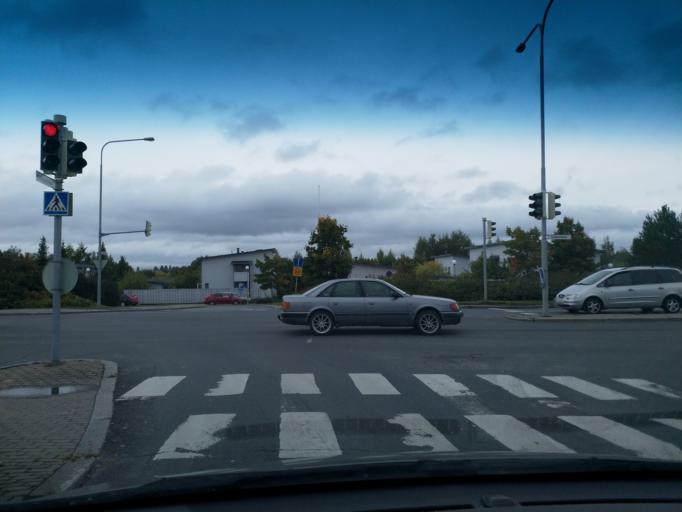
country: FI
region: Pirkanmaa
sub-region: Tampere
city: Tampere
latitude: 61.4783
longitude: 23.8413
